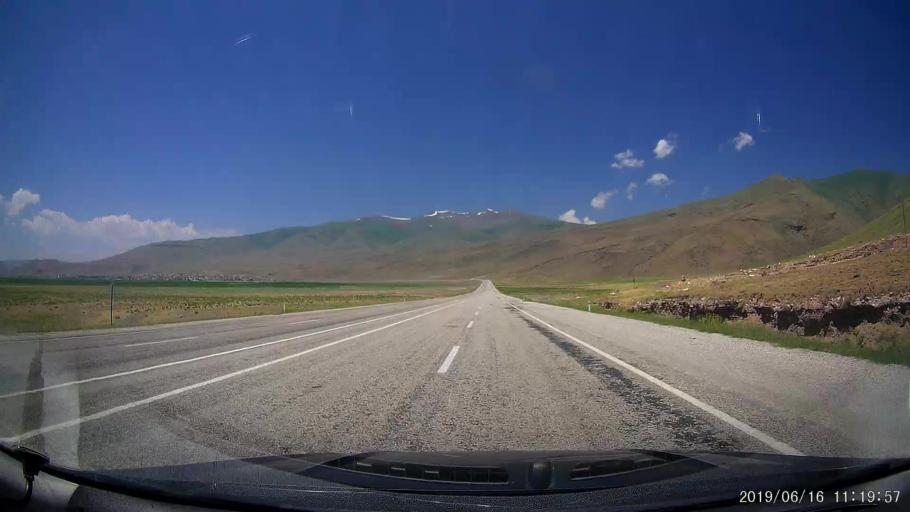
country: TR
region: Agri
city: Dogubayazit
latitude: 39.6964
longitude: 44.1024
